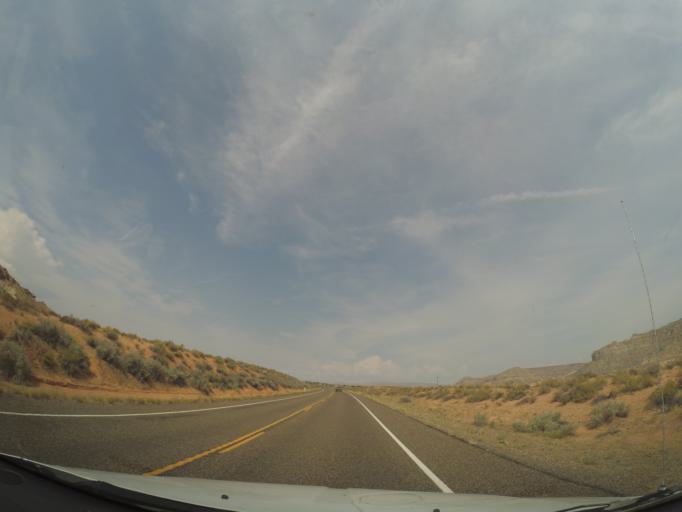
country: US
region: Arizona
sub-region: Coconino County
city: Page
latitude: 37.0494
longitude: -111.6257
